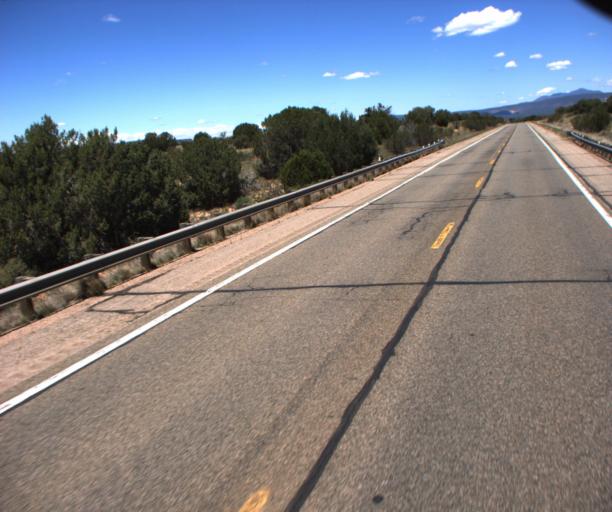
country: US
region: Arizona
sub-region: Yavapai County
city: Paulden
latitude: 34.9544
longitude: -112.4194
